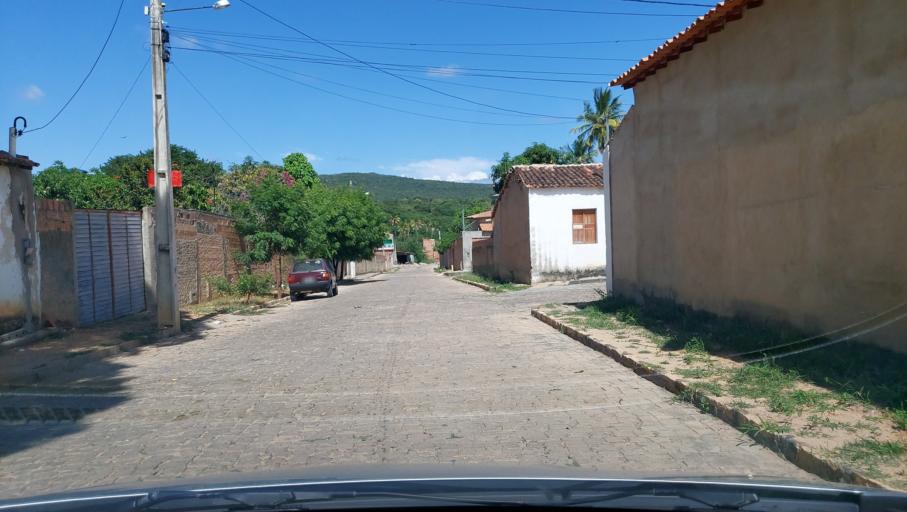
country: BR
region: Bahia
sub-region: Oliveira Dos Brejinhos
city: Beira Rio
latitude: -11.9968
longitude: -42.6298
